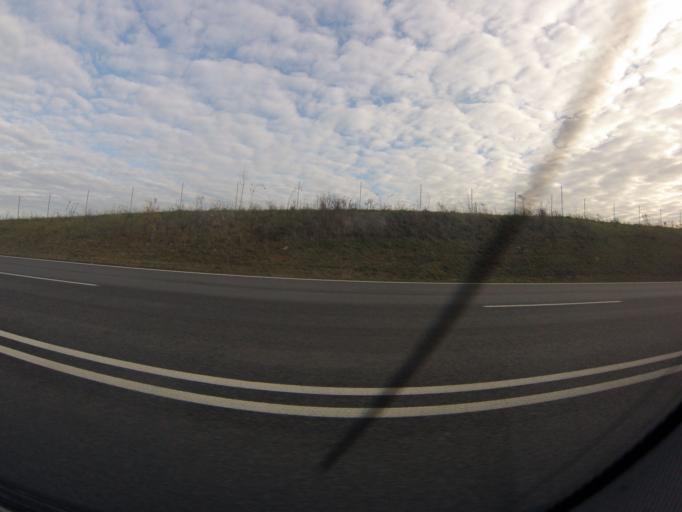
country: DE
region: Thuringia
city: Gossnitz
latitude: 50.8815
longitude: 12.4418
